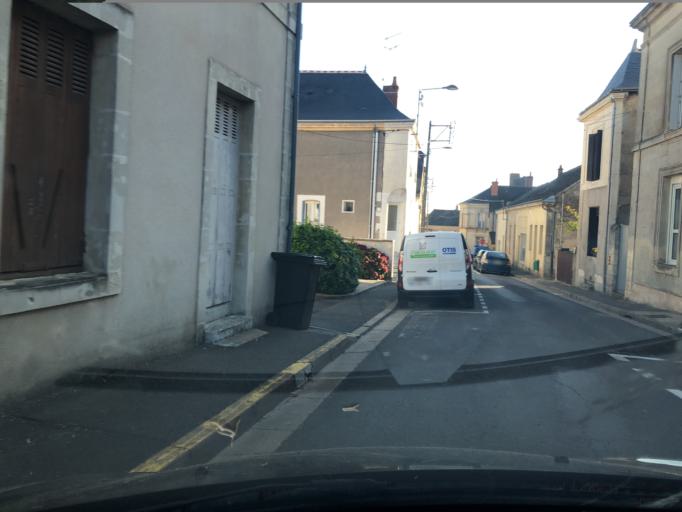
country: FR
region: Centre
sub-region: Departement d'Indre-et-Loire
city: Neuvy-le-Roi
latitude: 47.6038
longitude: 0.5954
